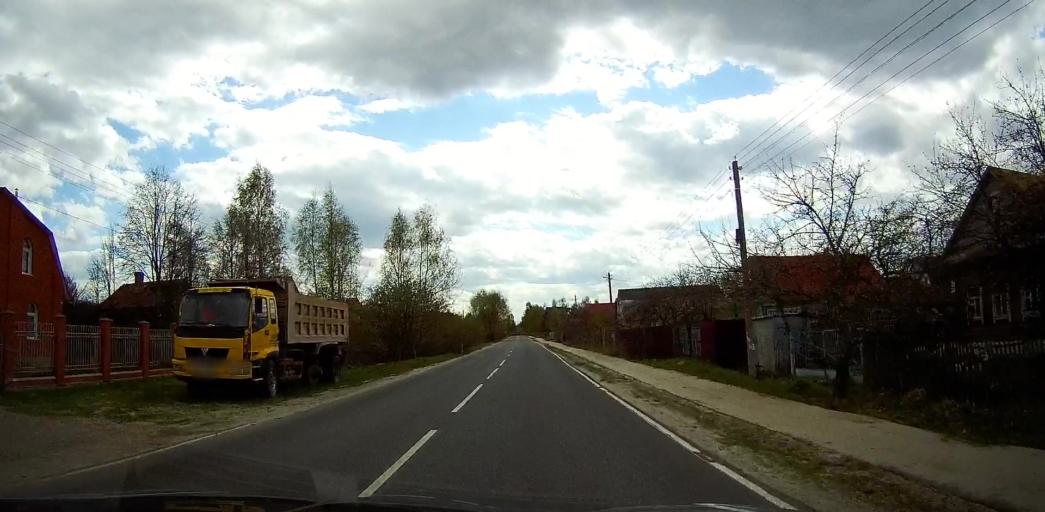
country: RU
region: Moskovskaya
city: Davydovo
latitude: 55.6637
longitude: 38.7577
